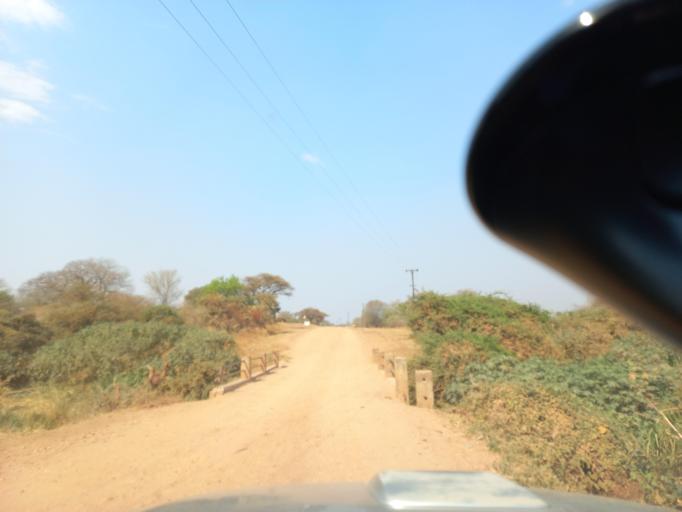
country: ZW
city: Chirundu
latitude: -15.9303
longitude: 28.9642
